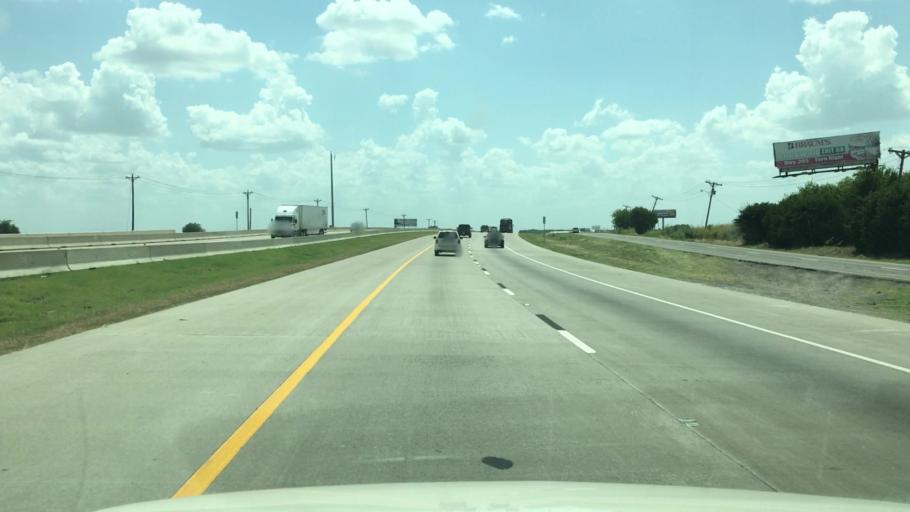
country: US
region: Texas
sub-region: Rockwall County
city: Fate
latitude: 32.9314
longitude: -96.3836
